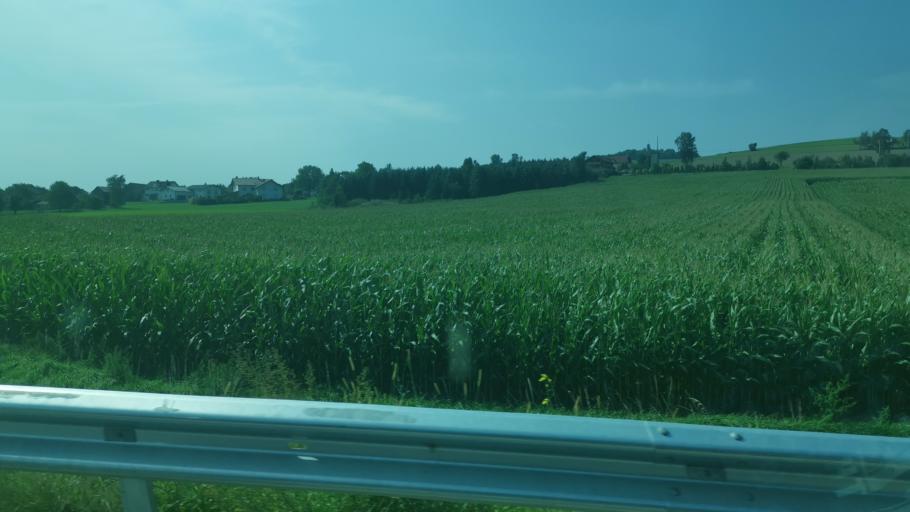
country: DE
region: Bavaria
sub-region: Upper Palatinate
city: Willmering
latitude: 49.2430
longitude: 12.6708
